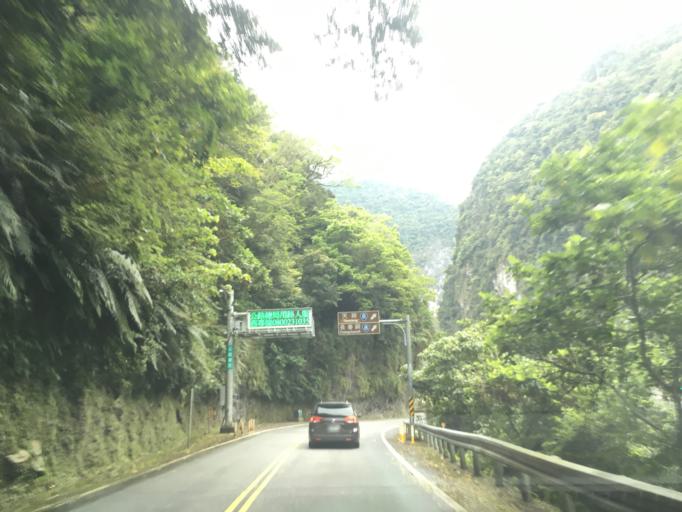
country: TW
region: Taiwan
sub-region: Hualien
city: Hualian
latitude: 24.1592
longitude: 121.6116
